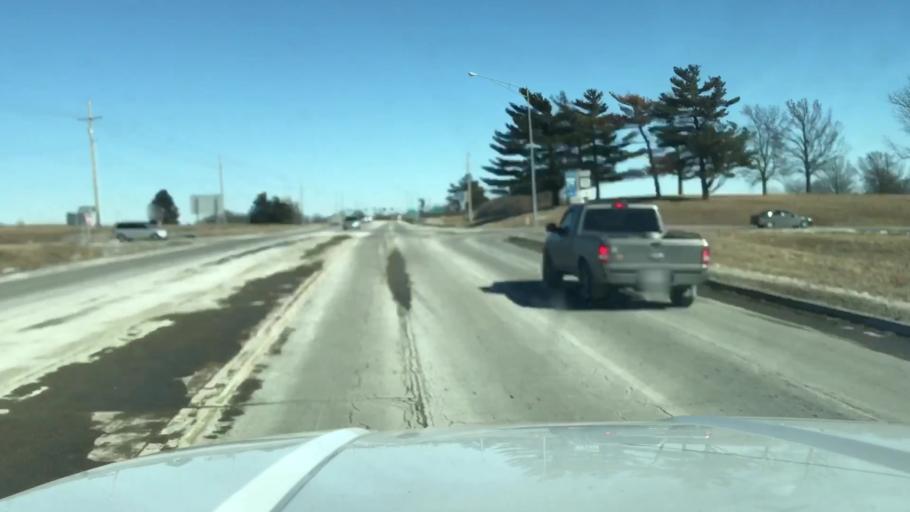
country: US
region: Missouri
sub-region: Andrew County
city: Country Club Village
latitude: 39.8133
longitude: -94.8053
